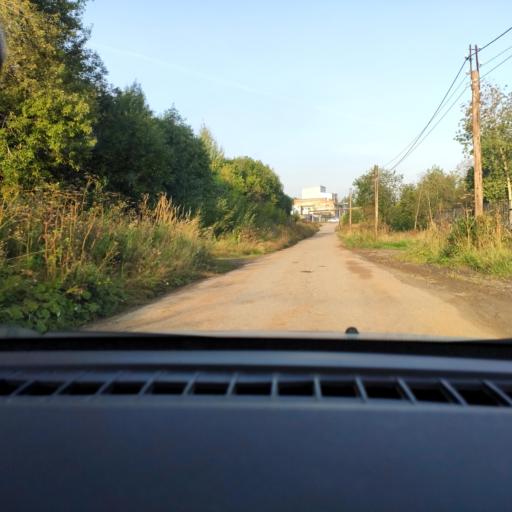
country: RU
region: Perm
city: Perm
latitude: 58.0711
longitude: 56.3743
